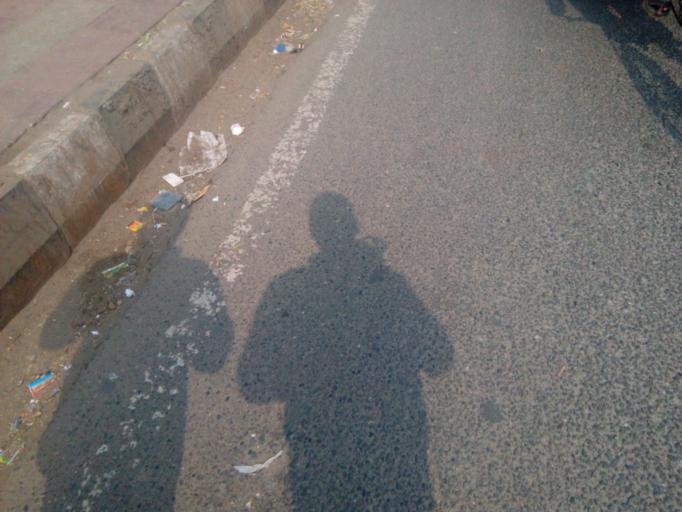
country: IN
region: Uttar Pradesh
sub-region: Gautam Buddha Nagar
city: Noida
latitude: 28.6444
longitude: 77.3166
